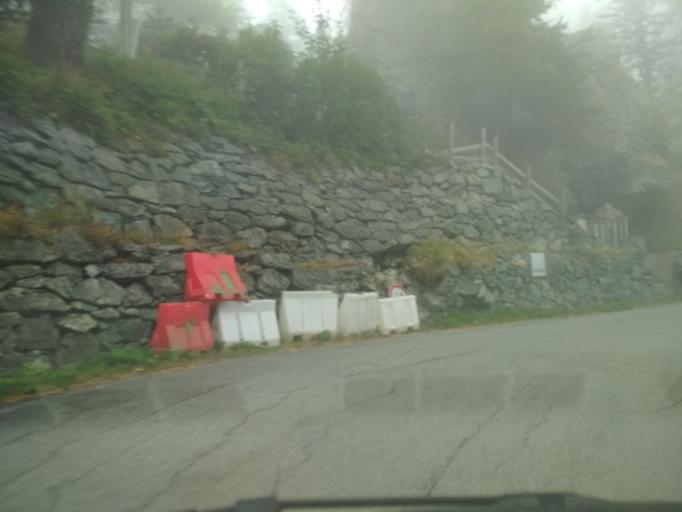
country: IT
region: Piedmont
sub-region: Provincia di Torino
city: Balme
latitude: 45.3024
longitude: 7.1928
